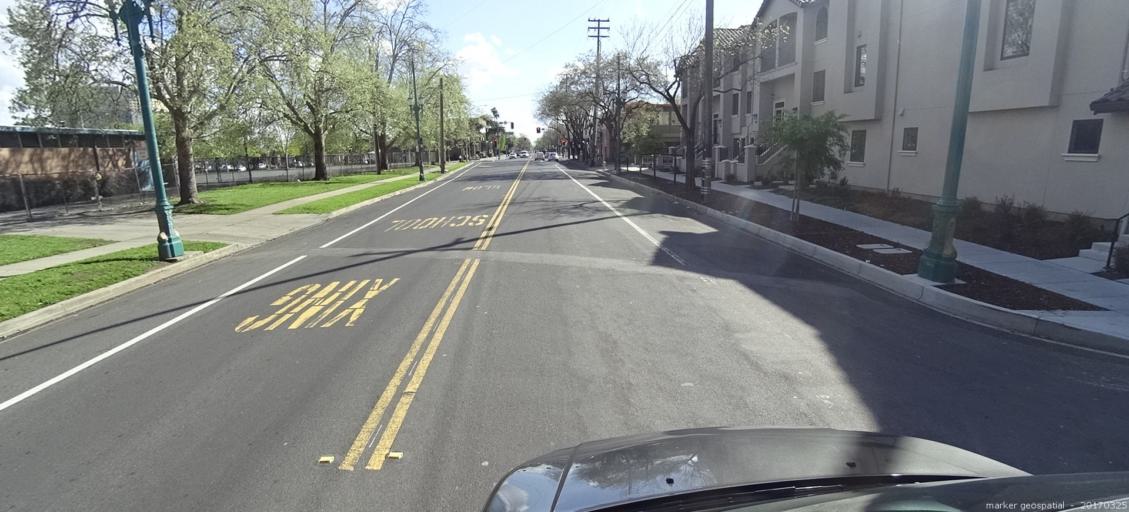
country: US
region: California
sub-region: Sacramento County
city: Sacramento
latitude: 38.5739
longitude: -121.4648
